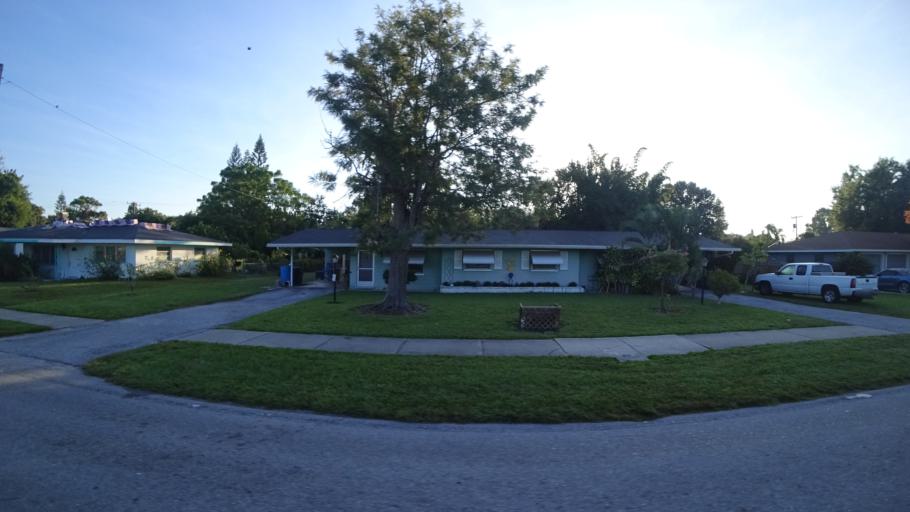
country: US
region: Florida
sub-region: Manatee County
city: South Bradenton
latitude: 27.4600
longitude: -82.5820
